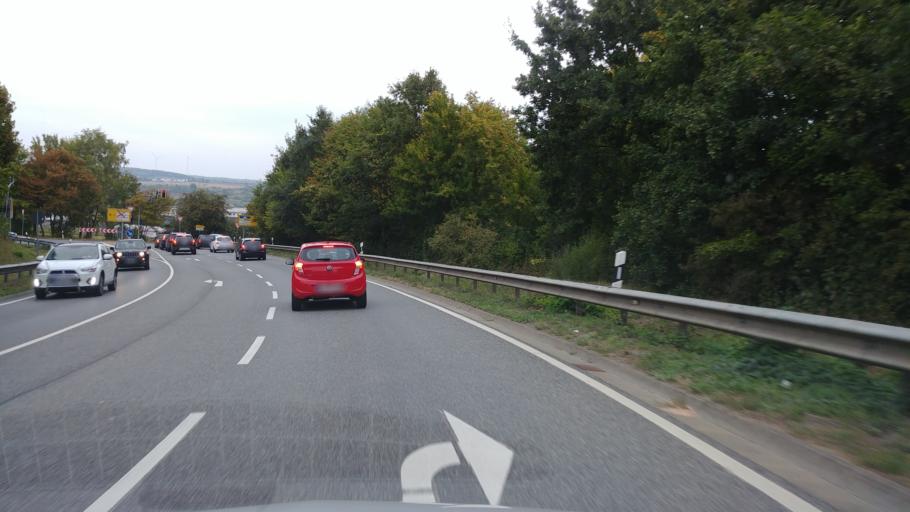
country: DE
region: Hesse
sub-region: Regierungsbezirk Giessen
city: Limburg an der Lahn
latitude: 50.3722
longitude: 8.0396
